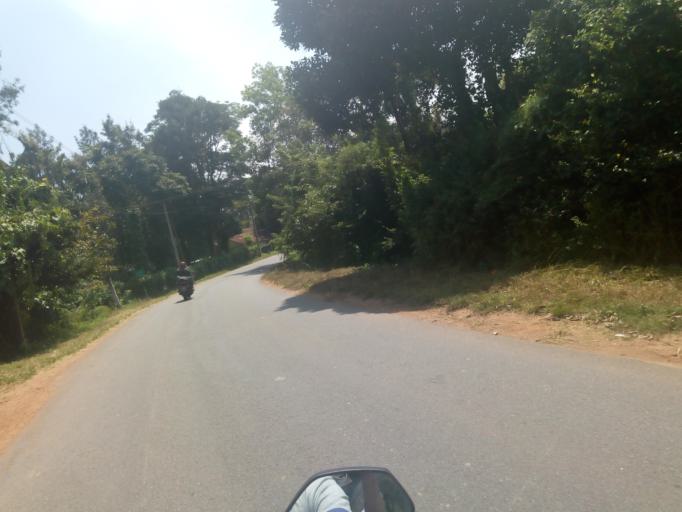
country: IN
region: Karnataka
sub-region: Kodagu
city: Ponnampet
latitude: 12.1096
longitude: 75.9419
